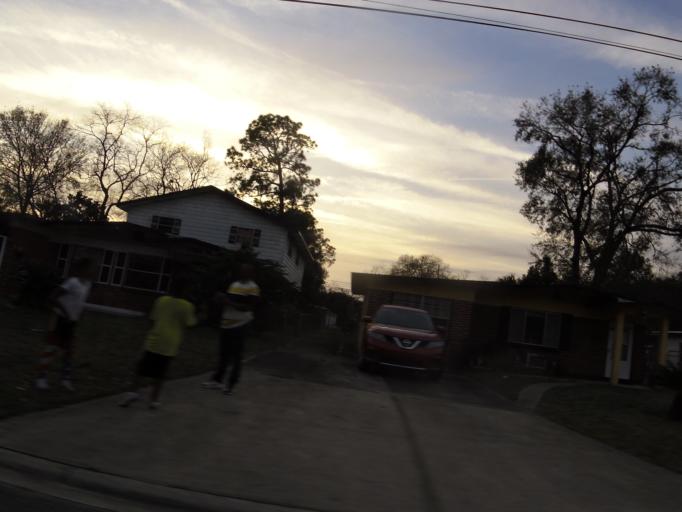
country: US
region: Florida
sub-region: Duval County
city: Jacksonville
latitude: 30.3587
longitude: -81.7051
